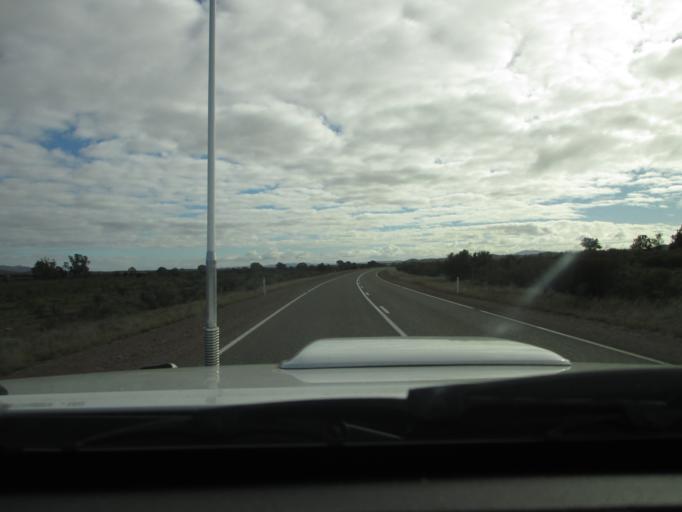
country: AU
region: South Australia
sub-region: Flinders Ranges
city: Quorn
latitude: -32.4628
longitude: 138.5379
